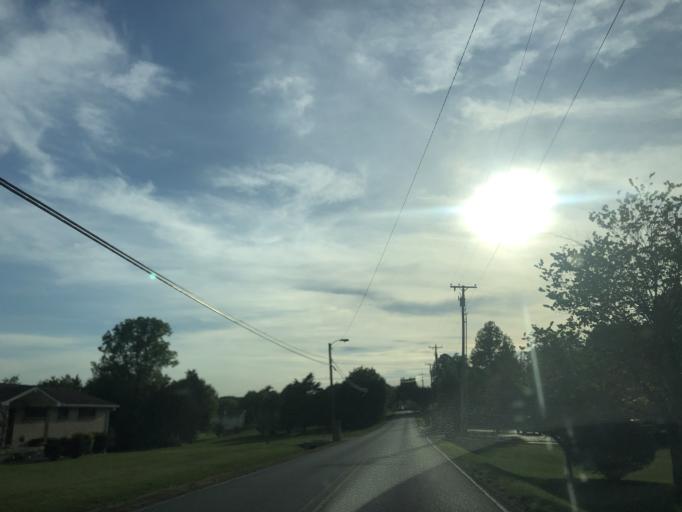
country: US
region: Tennessee
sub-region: Davidson County
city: Nashville
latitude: 36.2164
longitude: -86.8581
